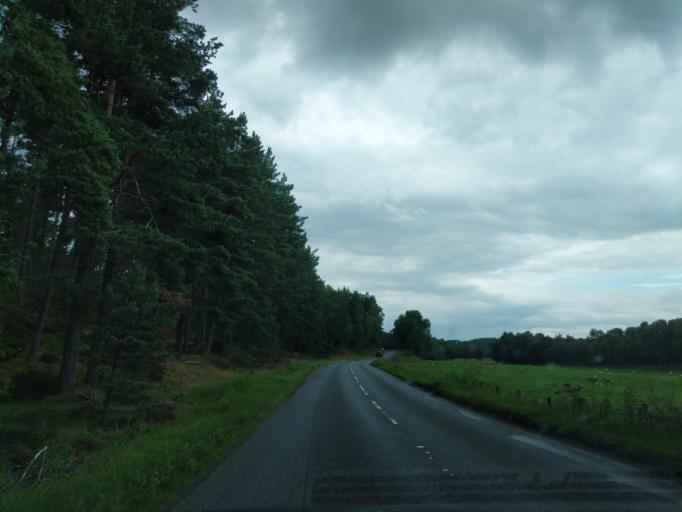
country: GB
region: Scotland
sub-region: Highland
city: Aviemore
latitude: 57.2924
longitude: -3.7912
